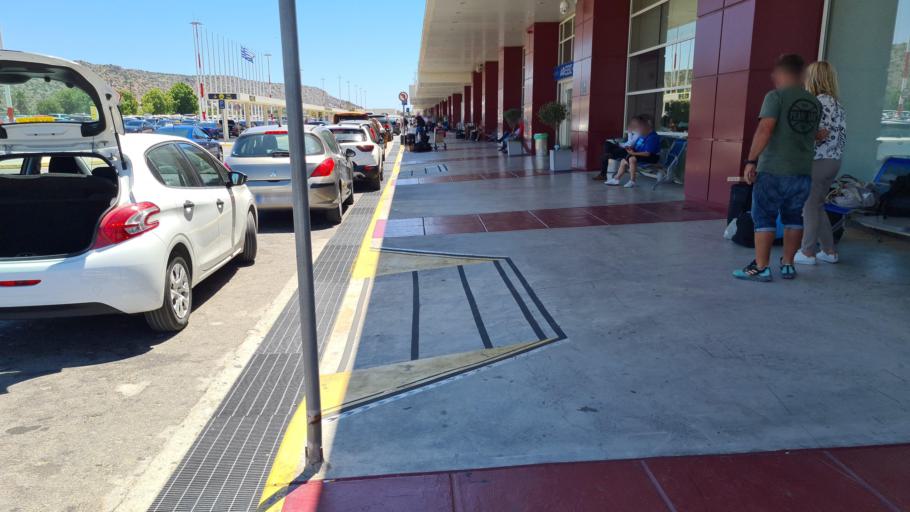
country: GR
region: Crete
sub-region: Nomos Chanias
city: Mouzouras
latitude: 35.5404
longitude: 24.1394
